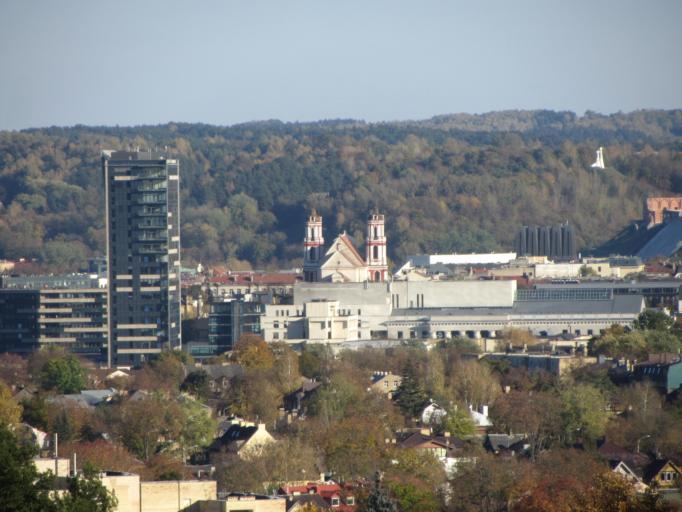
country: LT
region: Vilnius County
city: Justiniskes
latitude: 54.6948
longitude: 25.2293
